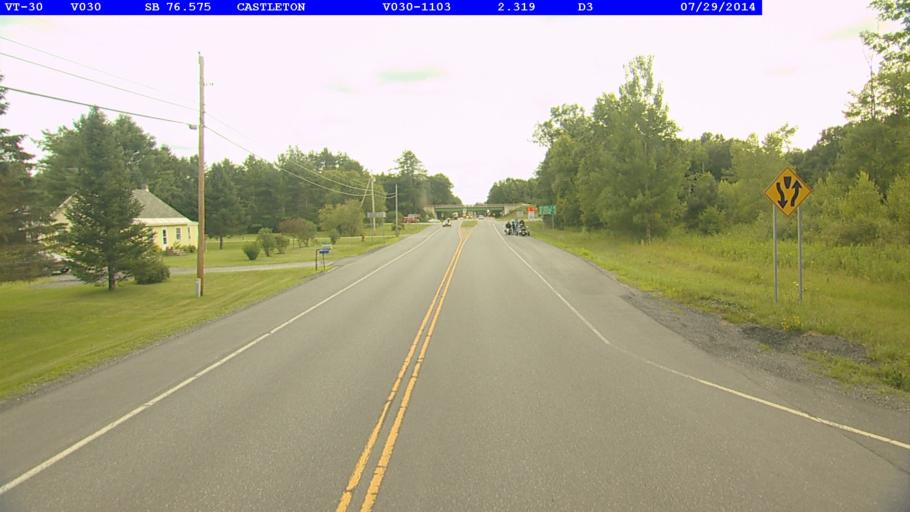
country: US
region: Vermont
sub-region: Rutland County
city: Castleton
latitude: 43.6200
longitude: -73.2059
